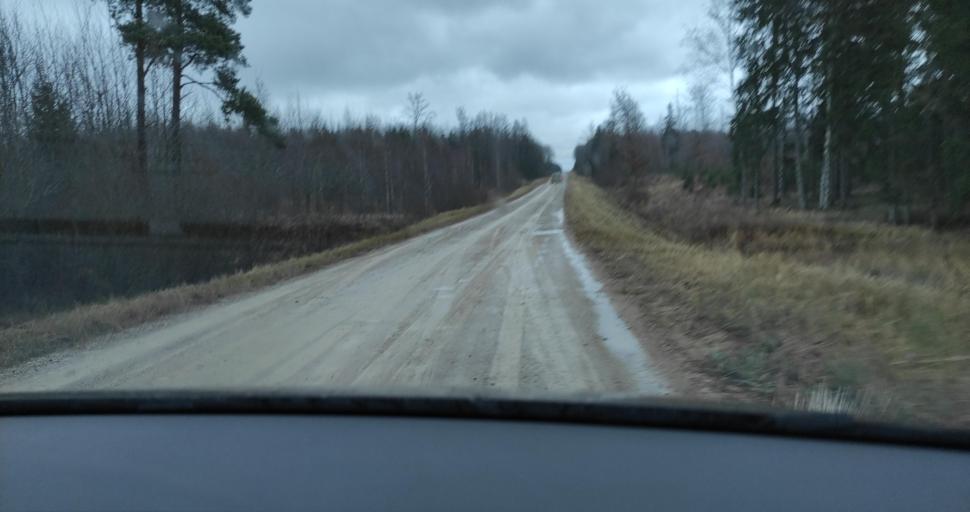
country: LV
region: Skrunda
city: Skrunda
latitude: 56.5557
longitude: 22.0908
